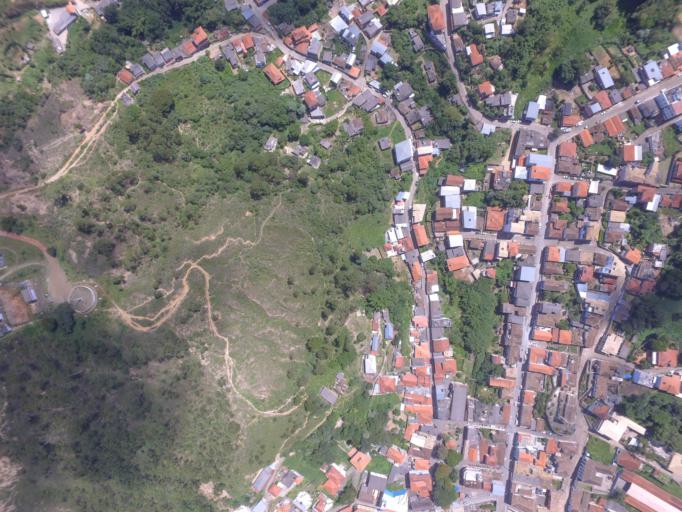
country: BR
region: Minas Gerais
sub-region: Tiradentes
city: Tiradentes
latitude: -21.0556
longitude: -44.0775
